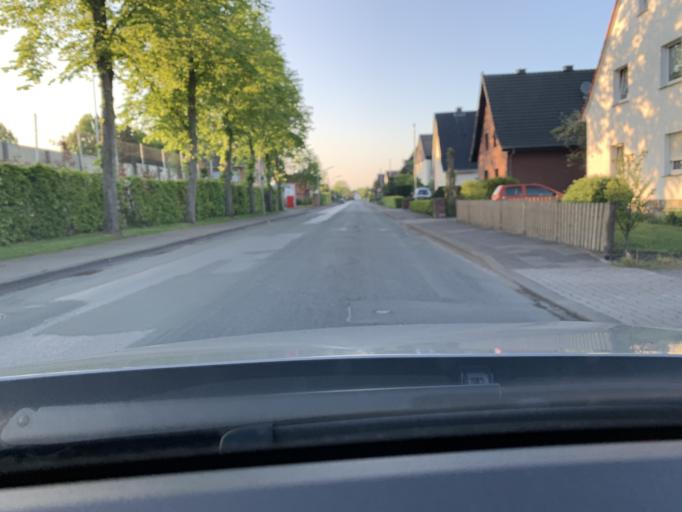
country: DE
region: North Rhine-Westphalia
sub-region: Regierungsbezirk Detmold
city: Rheda-Wiedenbruck
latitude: 51.8332
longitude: 8.3233
